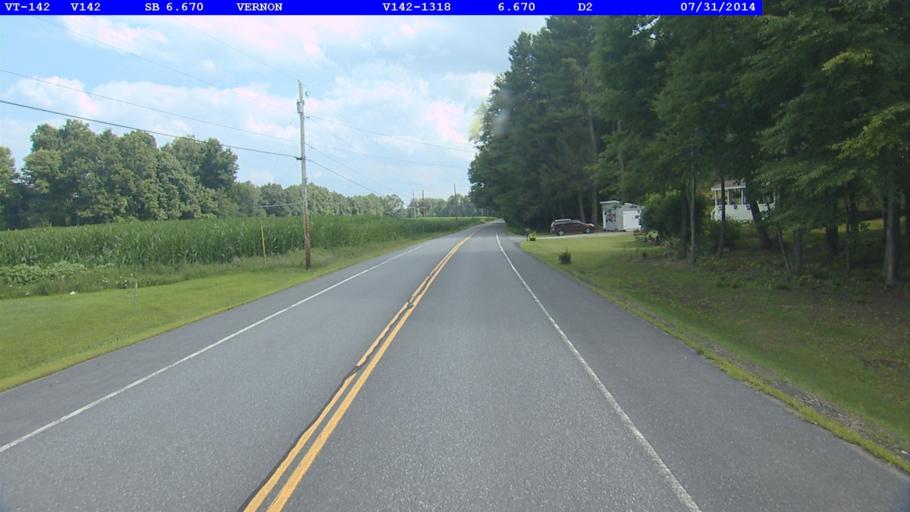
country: US
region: New Hampshire
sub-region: Cheshire County
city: Hinsdale
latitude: 42.7977
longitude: -72.5364
